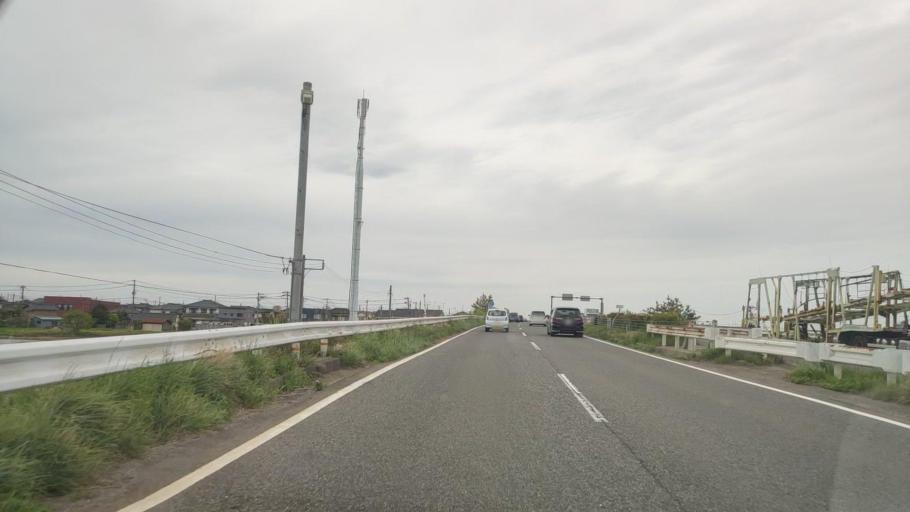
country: JP
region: Niigata
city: Kameda-honcho
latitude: 37.8612
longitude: 139.0922
